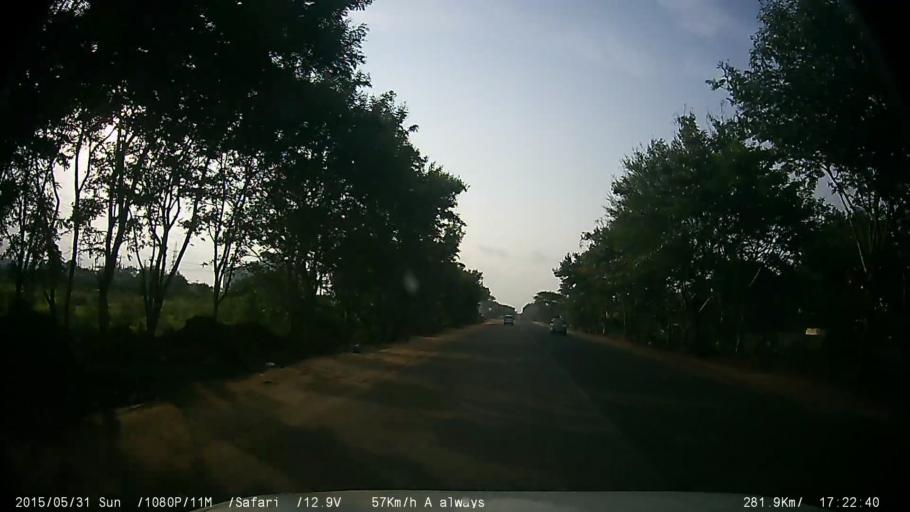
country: IN
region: Karnataka
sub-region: Chamrajnagar
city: Gundlupet
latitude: 11.8328
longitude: 76.6773
